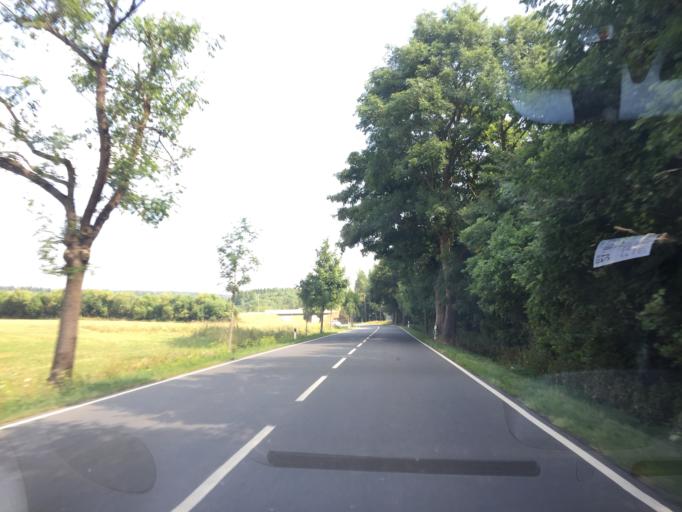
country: DE
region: Saxony-Anhalt
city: Elbingerode
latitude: 51.7581
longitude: 10.7823
